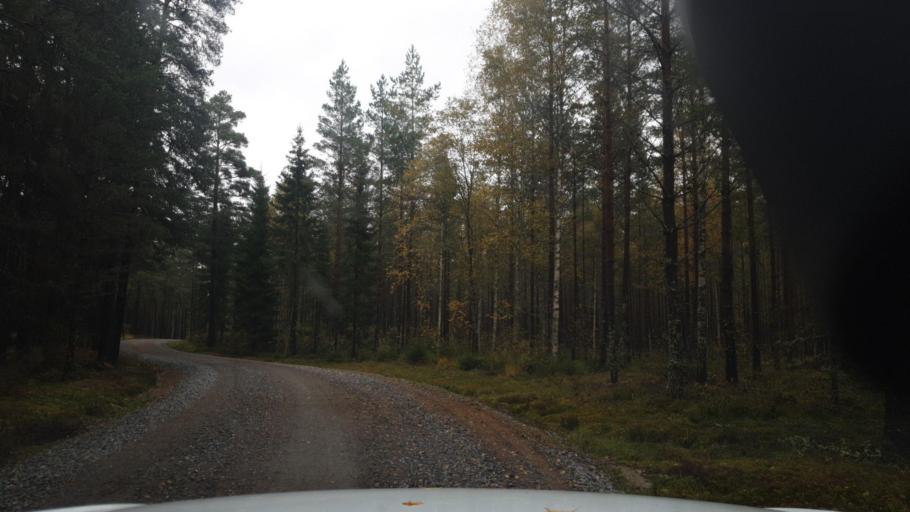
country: SE
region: Vaermland
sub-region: Karlstads Kommun
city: Edsvalla
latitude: 59.4563
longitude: 13.0974
